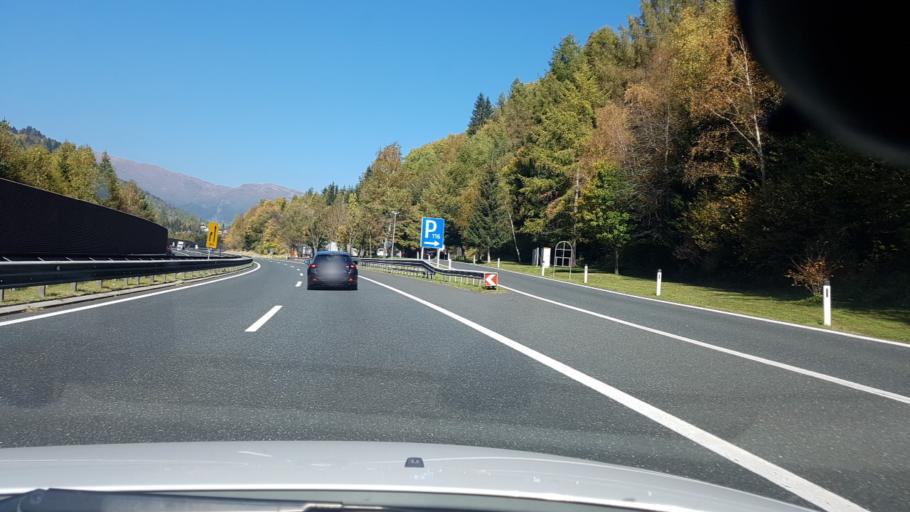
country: AT
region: Salzburg
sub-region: Politischer Bezirk Tamsweg
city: Sankt Michael im Lungau
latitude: 46.9928
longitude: 13.6223
